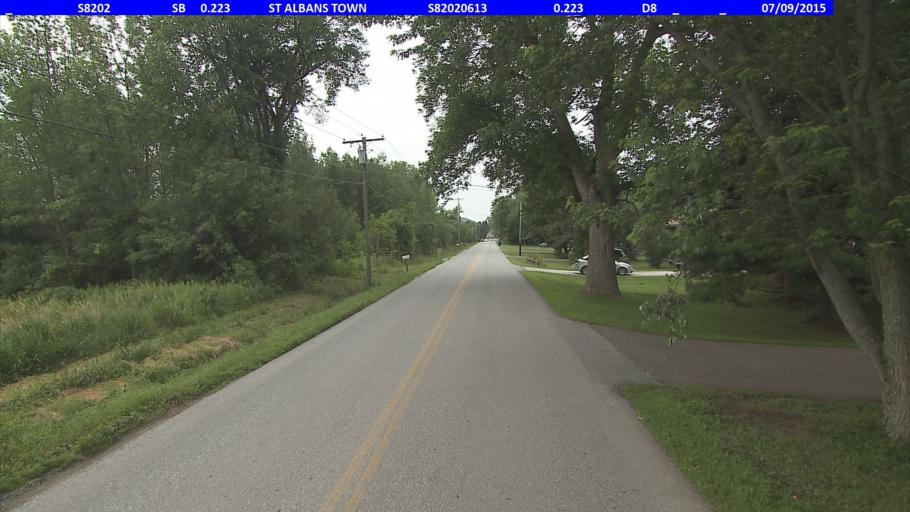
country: US
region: Vermont
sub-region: Franklin County
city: Saint Albans
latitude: 44.8152
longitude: -73.1075
